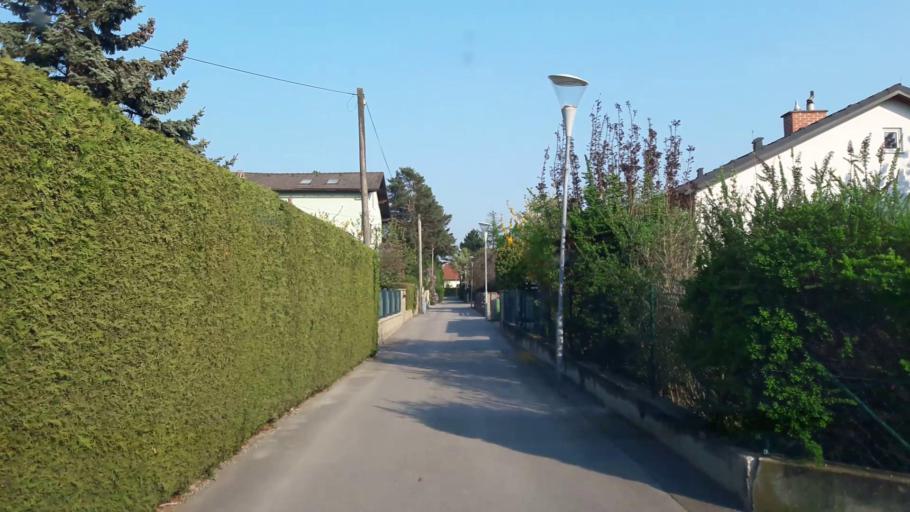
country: AT
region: Lower Austria
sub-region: Politischer Bezirk Ganserndorf
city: Deutsch-Wagram
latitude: 48.3174
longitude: 16.5904
